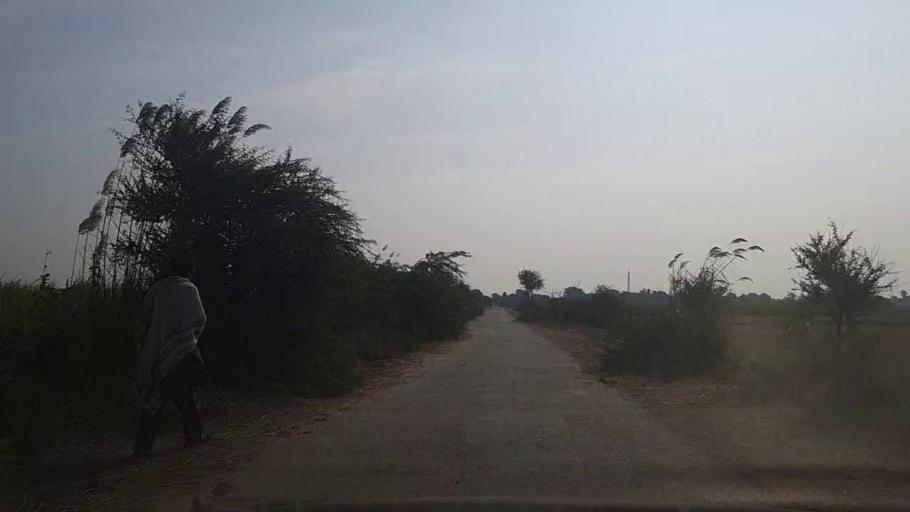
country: PK
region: Sindh
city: Bulri
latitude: 24.9719
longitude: 68.3272
